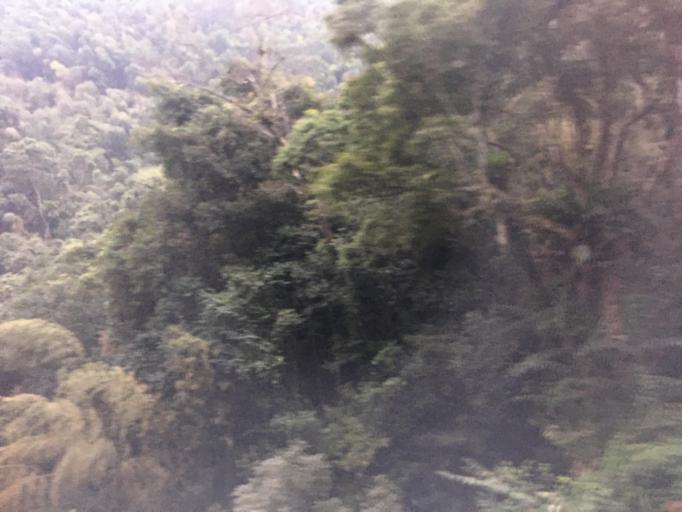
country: TW
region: Taiwan
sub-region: Chiayi
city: Jiayi Shi
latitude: 23.5253
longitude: 120.6519
